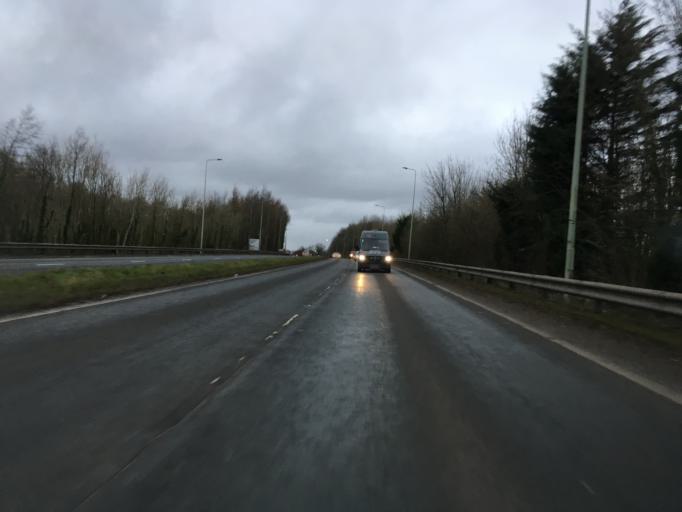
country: GB
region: Wales
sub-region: Rhondda Cynon Taf
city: Llantrisant
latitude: 51.5173
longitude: -3.3583
